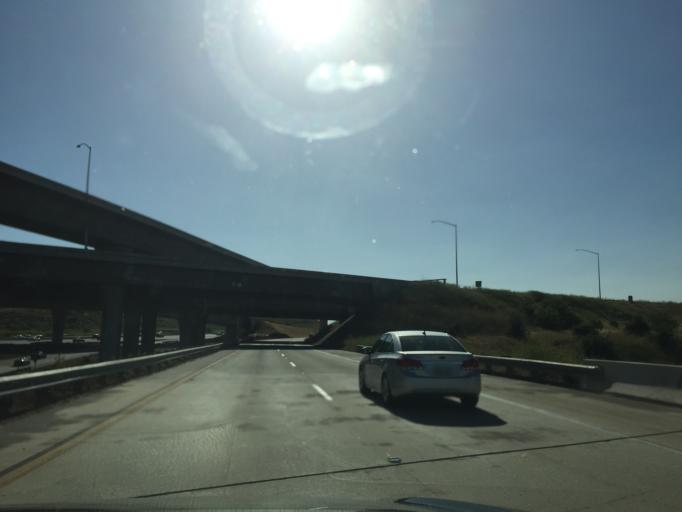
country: US
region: California
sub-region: Los Angeles County
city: Pomona
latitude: 34.0242
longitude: -117.7489
